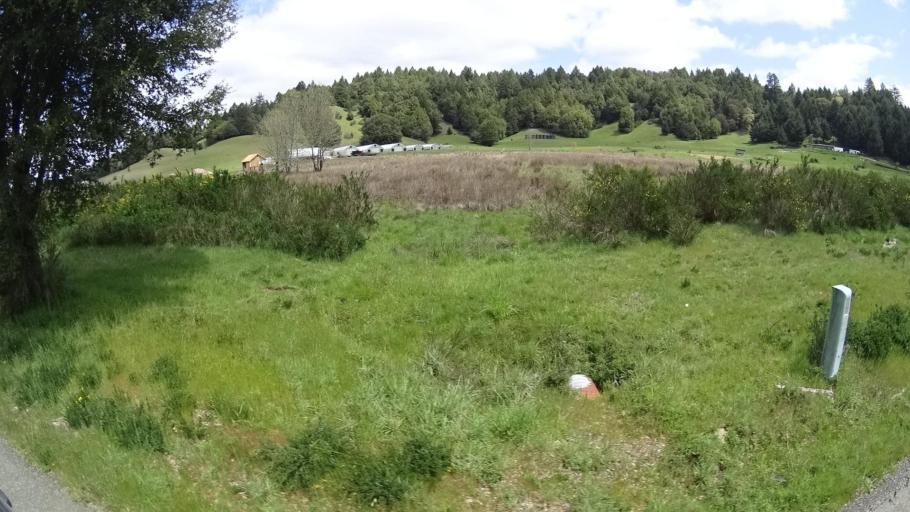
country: US
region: California
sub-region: Humboldt County
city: Redway
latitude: 40.0372
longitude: -123.9556
